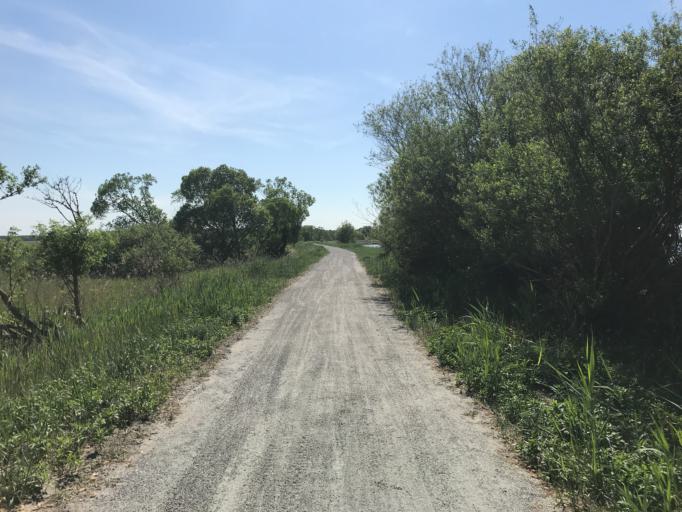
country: PL
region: West Pomeranian Voivodeship
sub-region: Powiat kamienski
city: Wolin
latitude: 53.7636
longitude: 14.6125
